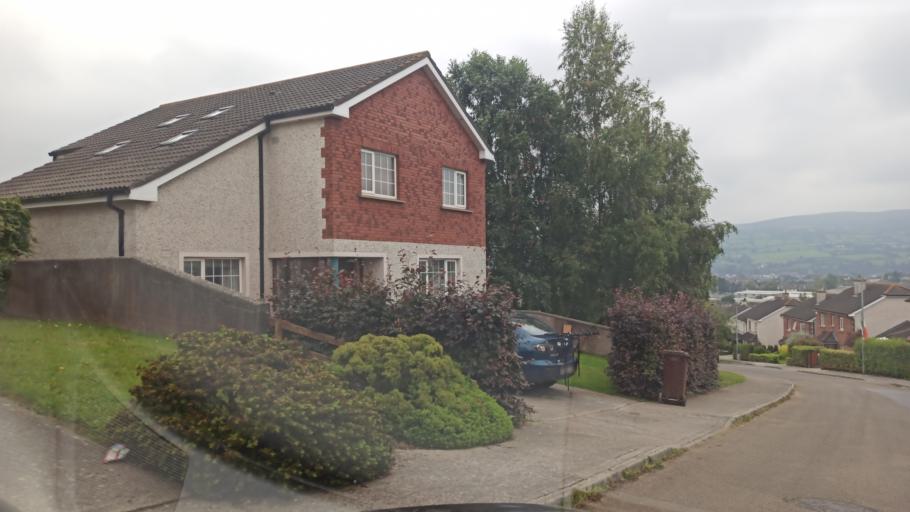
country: IE
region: Munster
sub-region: South Tipperary
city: Cluain Meala
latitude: 52.3679
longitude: -7.7147
